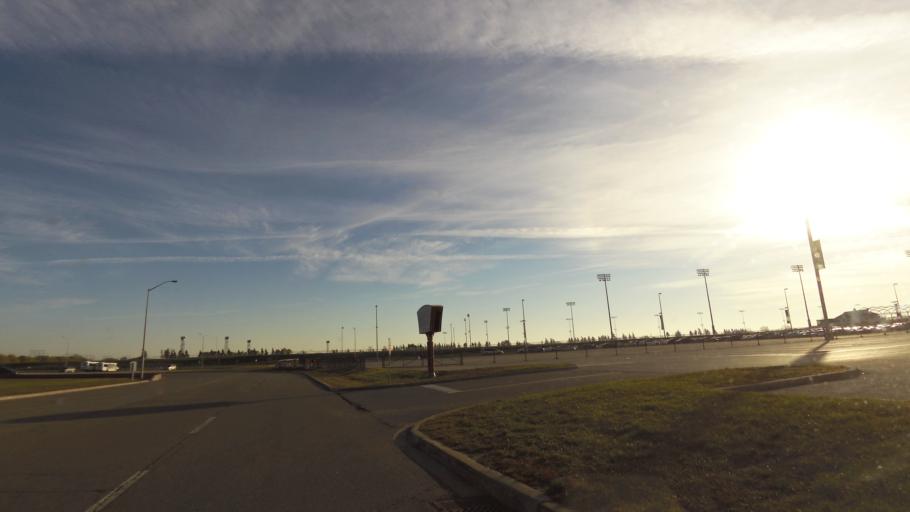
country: CA
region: Ontario
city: Etobicoke
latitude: 43.7165
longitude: -79.5991
